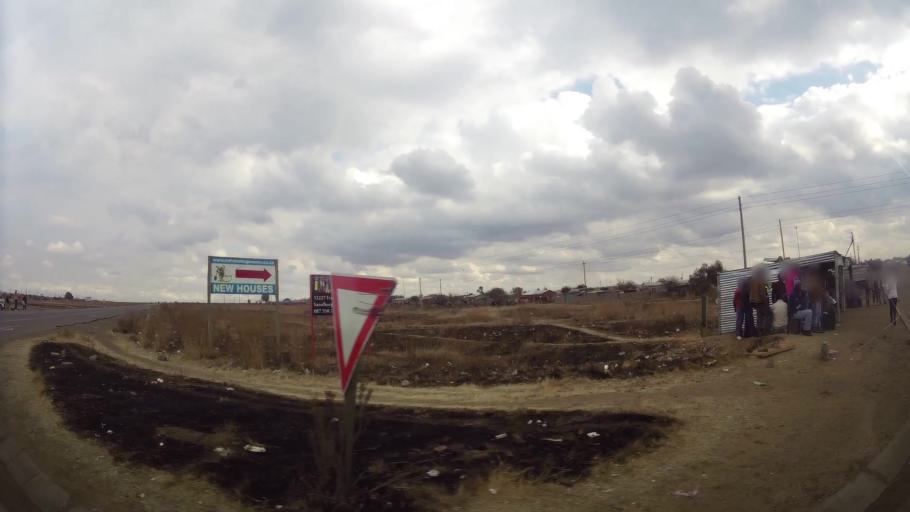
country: ZA
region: Orange Free State
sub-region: Fezile Dabi District Municipality
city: Sasolburg
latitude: -26.8564
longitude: 27.8881
